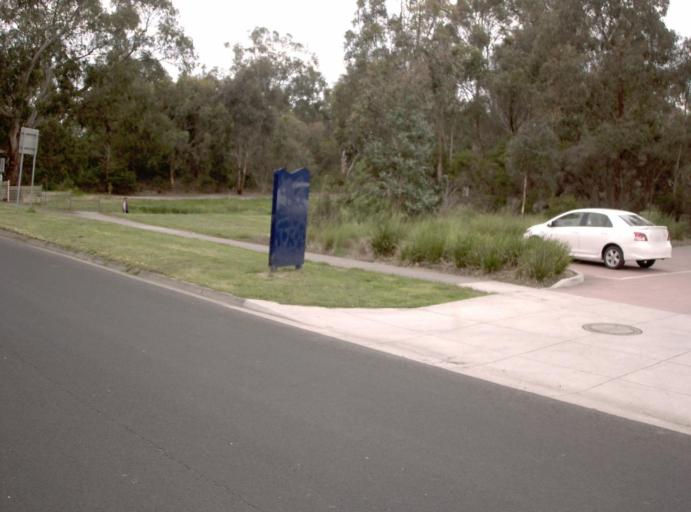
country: AU
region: Victoria
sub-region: Knox
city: Wantirna
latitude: -37.8399
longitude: 145.2274
